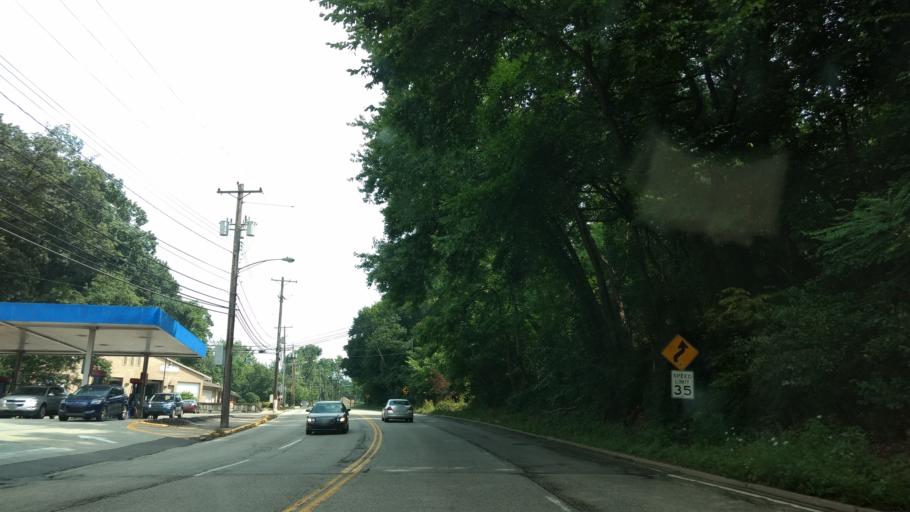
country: US
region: Pennsylvania
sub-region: Allegheny County
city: West View
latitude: 40.5467
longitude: -80.0290
